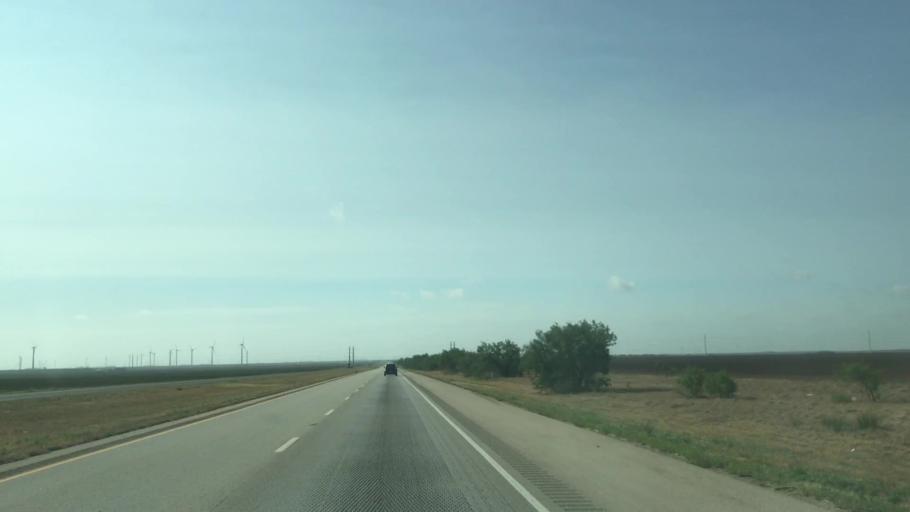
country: US
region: Texas
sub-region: Scurry County
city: Snyder
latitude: 32.6071
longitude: -100.7444
